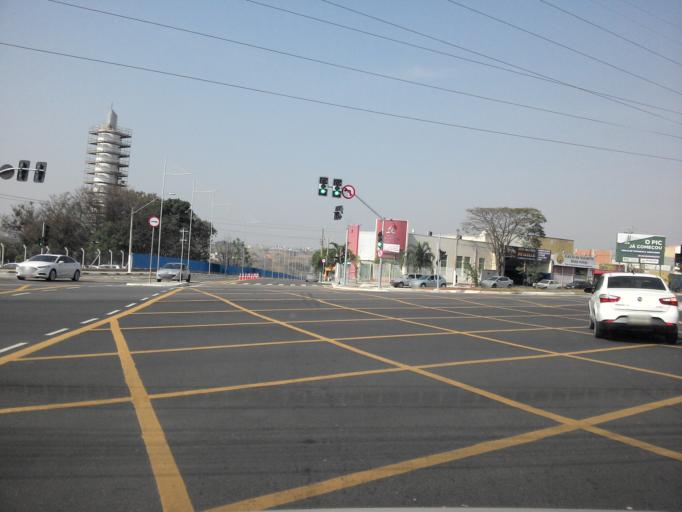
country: BR
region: Sao Paulo
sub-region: Hortolandia
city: Hortolandia
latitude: -22.8772
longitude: -47.1989
